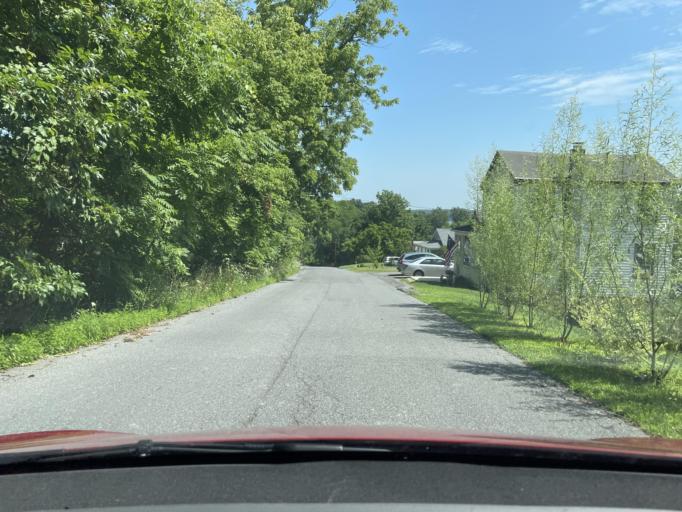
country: US
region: New York
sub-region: Ulster County
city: Saugerties South
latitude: 42.0687
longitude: -73.9459
